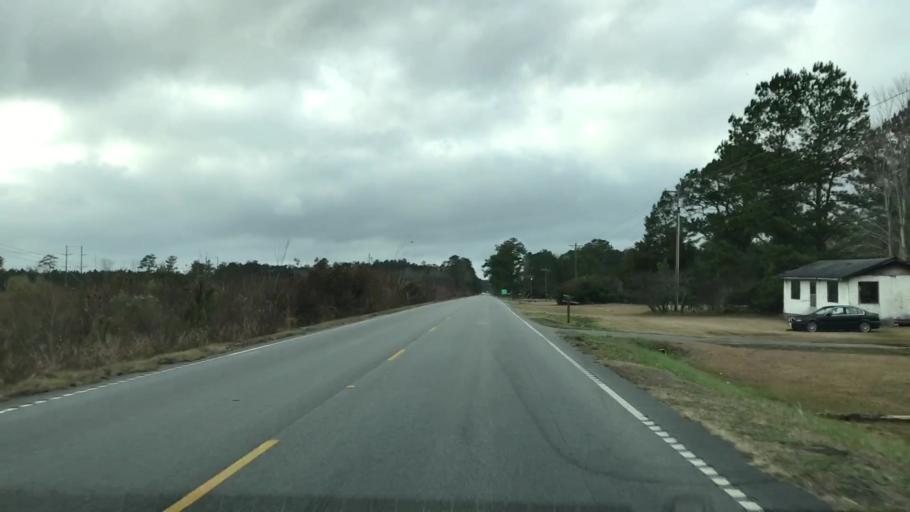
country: US
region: South Carolina
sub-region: Berkeley County
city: Saint Stephen
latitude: 33.2826
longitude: -79.7369
